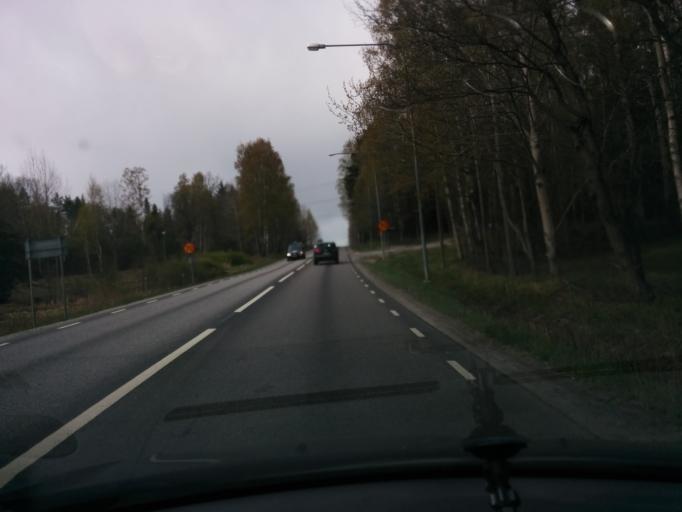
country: SE
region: Stockholm
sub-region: Botkyrka Kommun
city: Fittja
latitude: 59.2414
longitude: 17.8970
